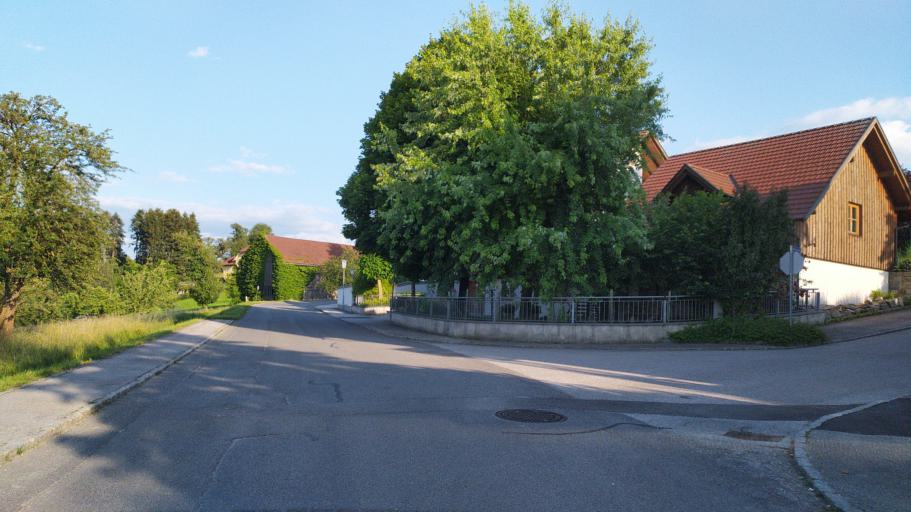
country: AT
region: Lower Austria
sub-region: Politischer Bezirk Amstetten
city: Strengberg
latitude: 48.1451
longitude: 14.6515
